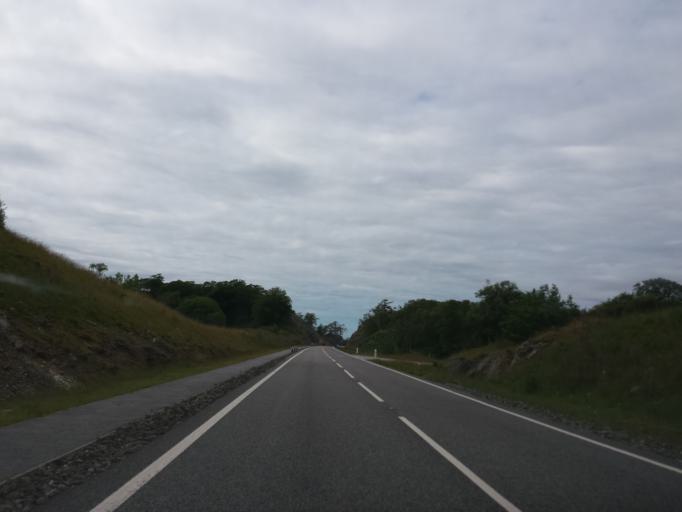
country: GB
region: Scotland
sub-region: Argyll and Bute
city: Isle Of Mull
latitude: 56.9041
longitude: -5.8140
